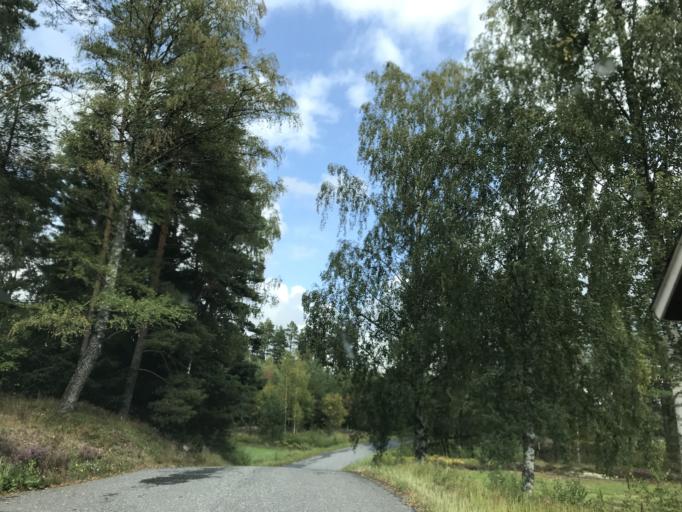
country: FI
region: Varsinais-Suomi
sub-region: Salo
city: Pernioe
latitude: 60.0735
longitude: 23.1155
